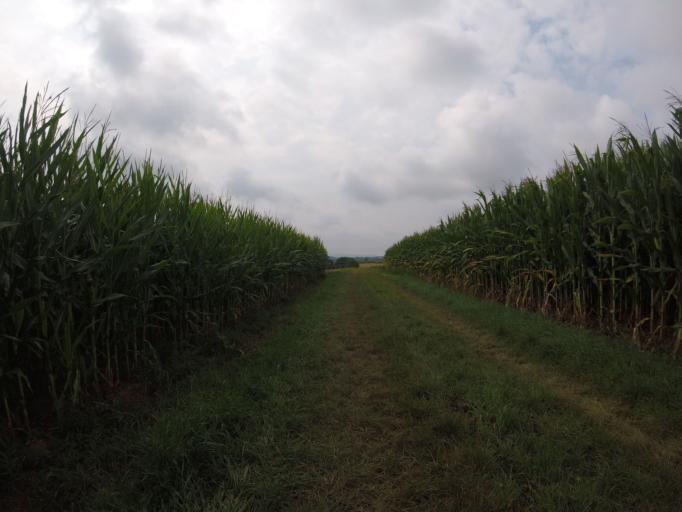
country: DE
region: Baden-Wuerttemberg
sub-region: Regierungsbezirk Stuttgart
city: Aspach
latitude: 48.9616
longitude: 9.3903
